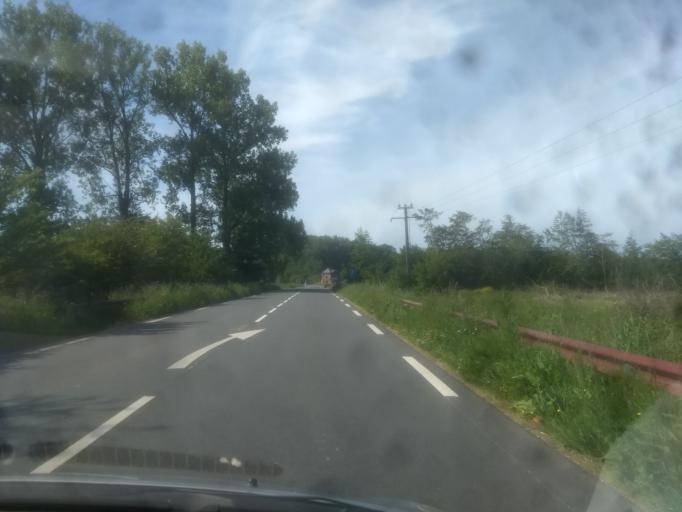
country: FR
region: Picardie
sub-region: Departement de la Somme
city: Doullens
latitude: 50.1663
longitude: 2.3014
